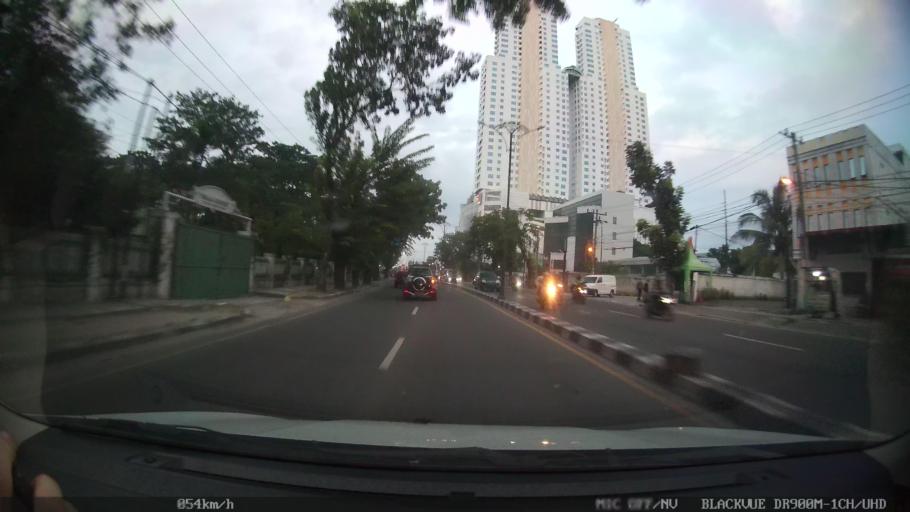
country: ID
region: North Sumatra
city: Sunggal
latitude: 3.5918
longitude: 98.6244
